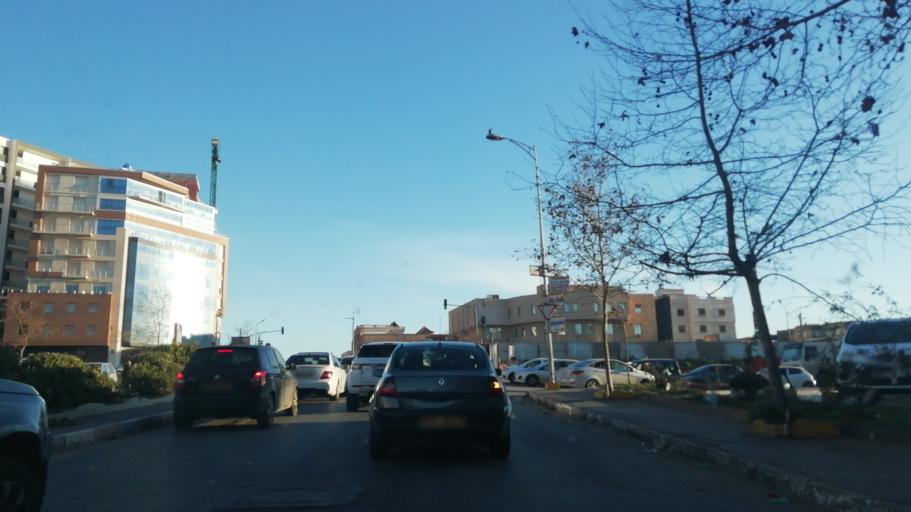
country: DZ
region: Oran
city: Bir el Djir
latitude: 35.7211
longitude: -0.5834
